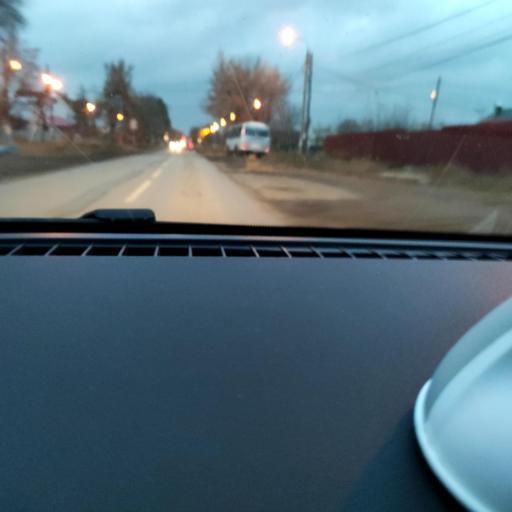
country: RU
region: Samara
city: Smyshlyayevka
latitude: 53.2458
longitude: 50.3376
